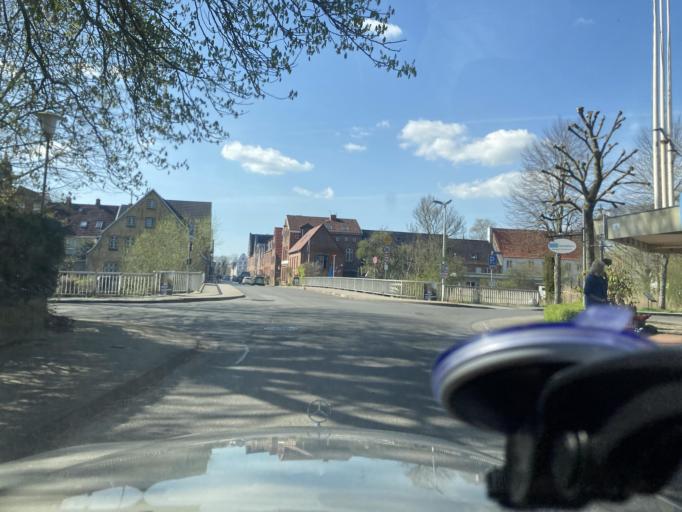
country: DE
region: Schleswig-Holstein
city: Friedrichstadt
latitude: 54.3751
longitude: 9.0917
